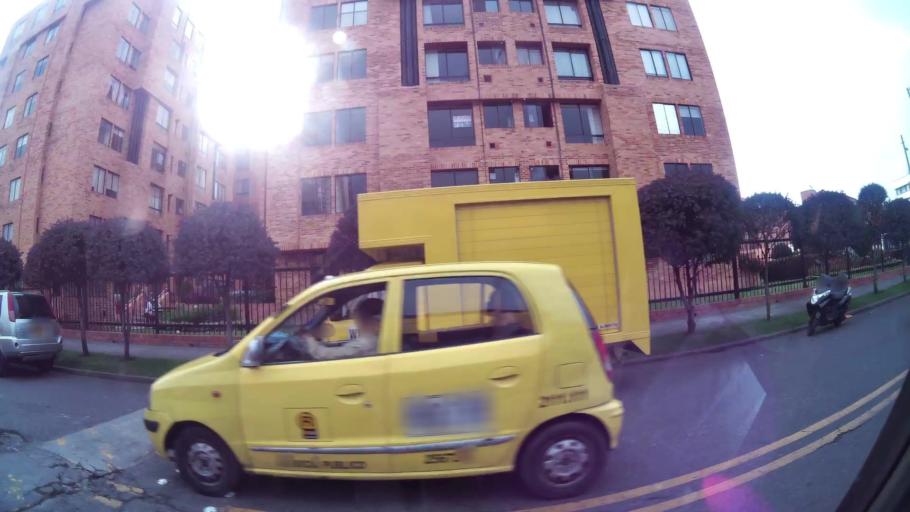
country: CO
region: Bogota D.C.
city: Barrio San Luis
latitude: 4.7267
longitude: -74.0616
